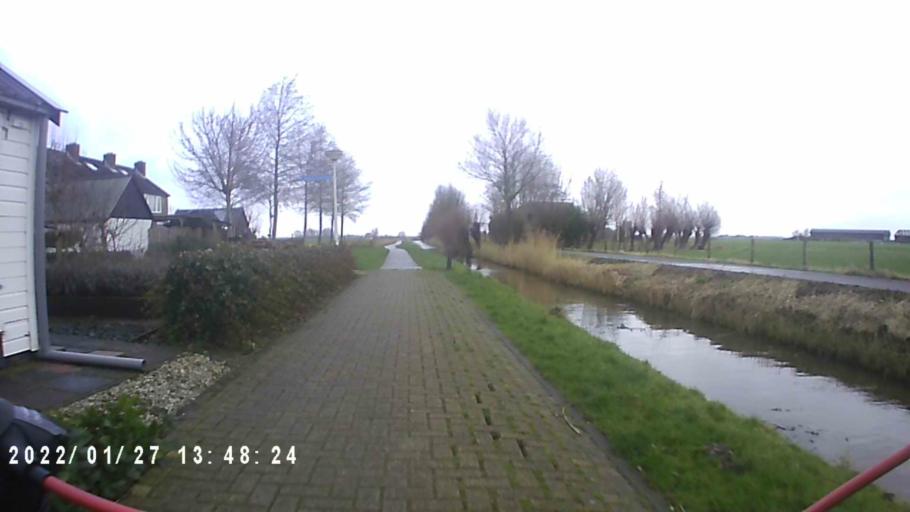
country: NL
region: Friesland
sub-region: Gemeente Kollumerland en Nieuwkruisland
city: Kollum
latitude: 53.3033
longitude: 6.1929
